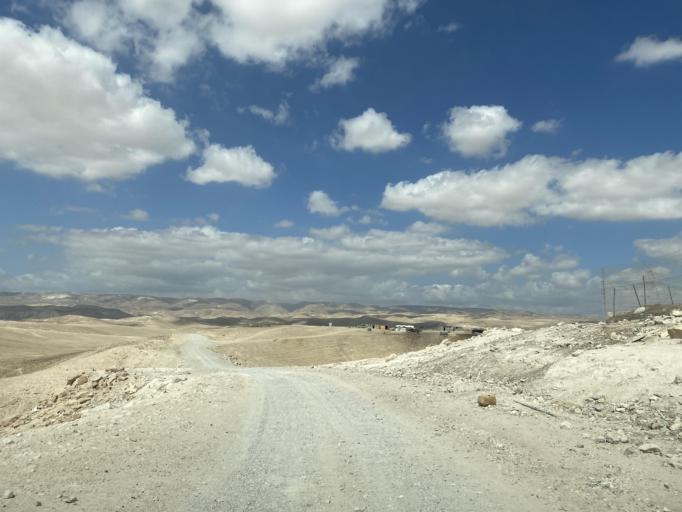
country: PS
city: `Arab ar Rashaydah
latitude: 31.5226
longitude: 35.3044
